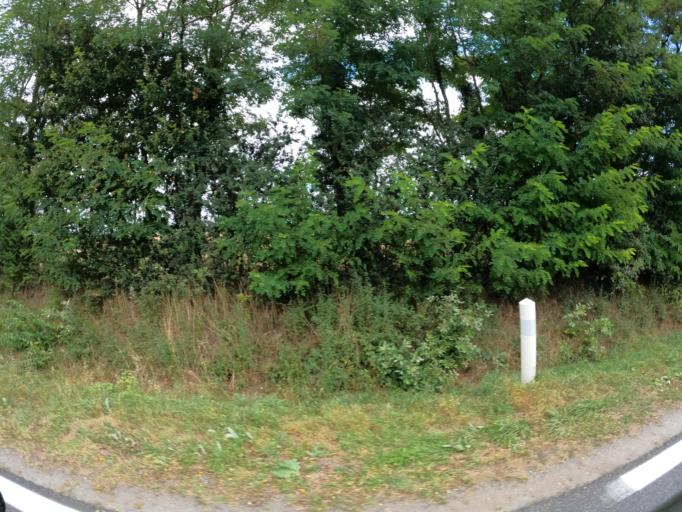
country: FR
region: Poitou-Charentes
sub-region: Departement de la Vienne
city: Charroux
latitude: 46.1553
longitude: 0.3687
